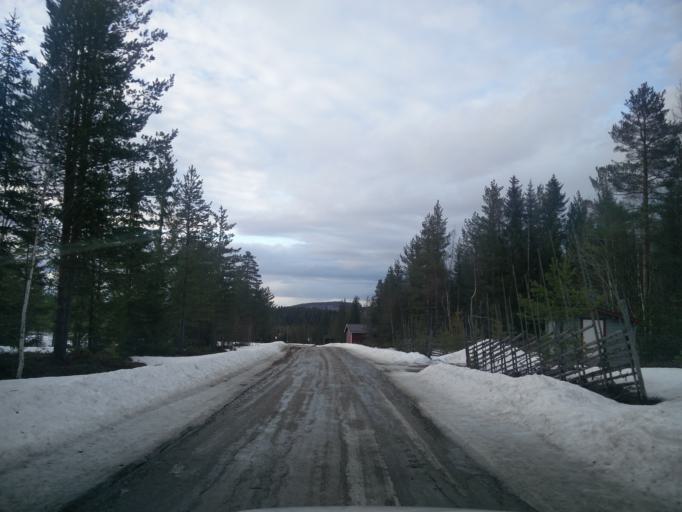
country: SE
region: Jaemtland
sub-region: Bergs Kommun
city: Hoverberg
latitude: 62.5042
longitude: 14.1796
